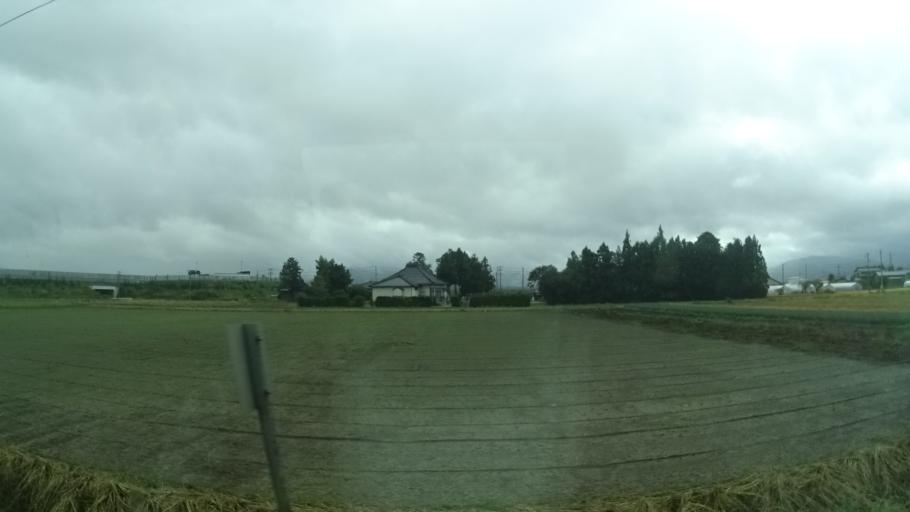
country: JP
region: Yamagata
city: Tsuruoka
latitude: 38.7427
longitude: 139.7767
